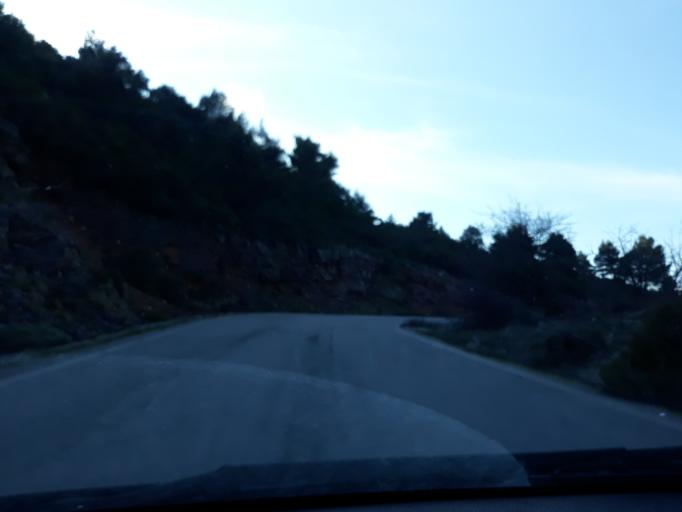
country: GR
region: Attica
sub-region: Nomarchia Dytikis Attikis
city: Fyli
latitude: 38.1574
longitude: 23.6292
